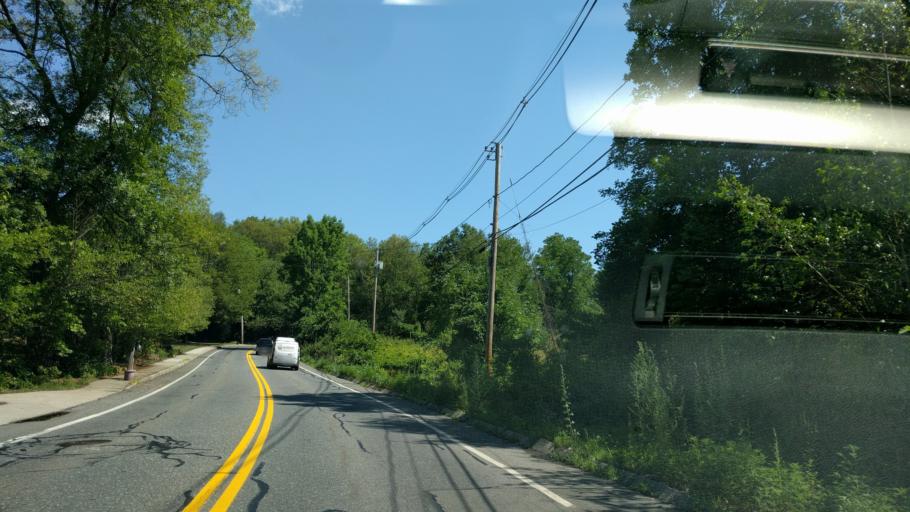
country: US
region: Massachusetts
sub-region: Middlesex County
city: Marlborough
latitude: 42.3358
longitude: -71.5295
